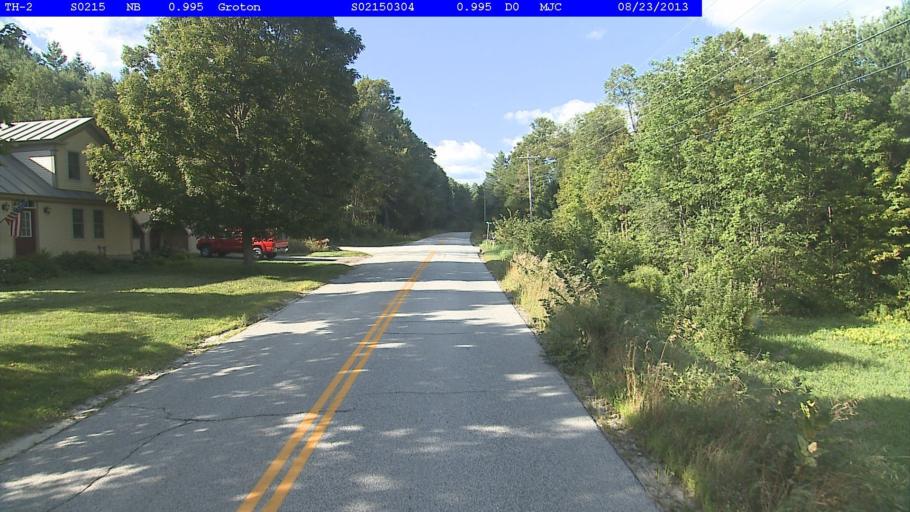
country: US
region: New Hampshire
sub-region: Grafton County
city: Woodsville
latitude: 44.2231
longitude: -72.1908
